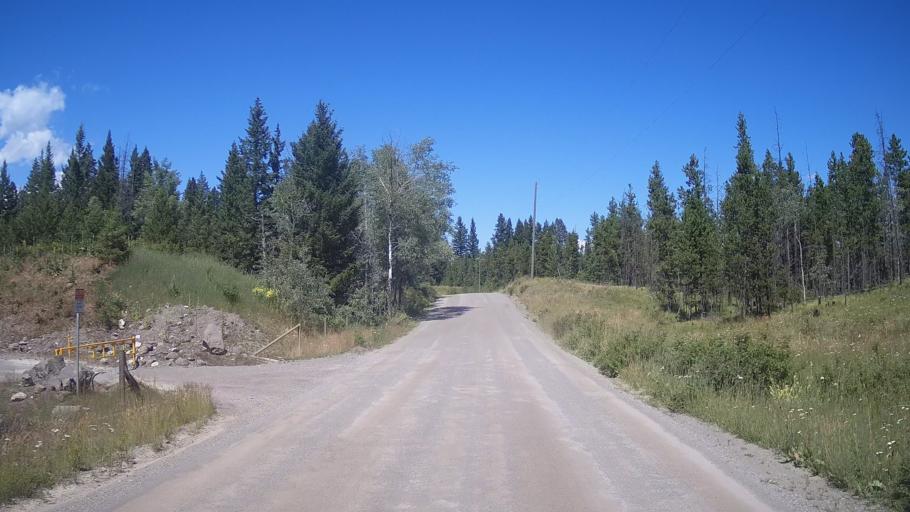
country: CA
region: British Columbia
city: Cache Creek
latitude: 51.2012
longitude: -121.5922
